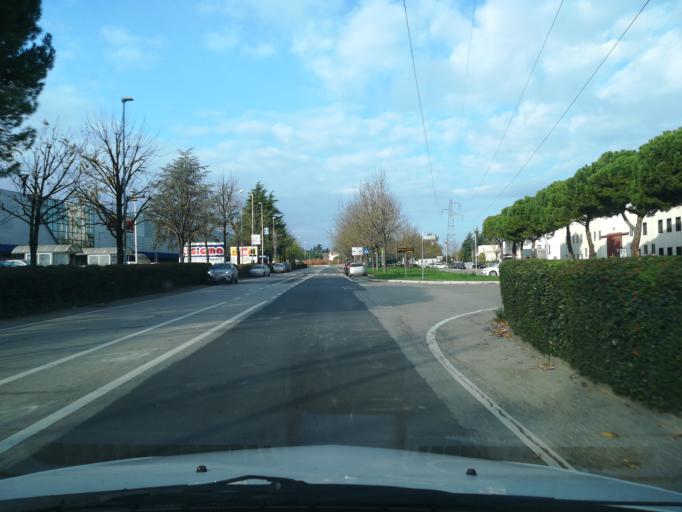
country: IT
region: Emilia-Romagna
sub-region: Provincia di Bologna
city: Imola
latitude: 44.3672
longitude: 11.7068
